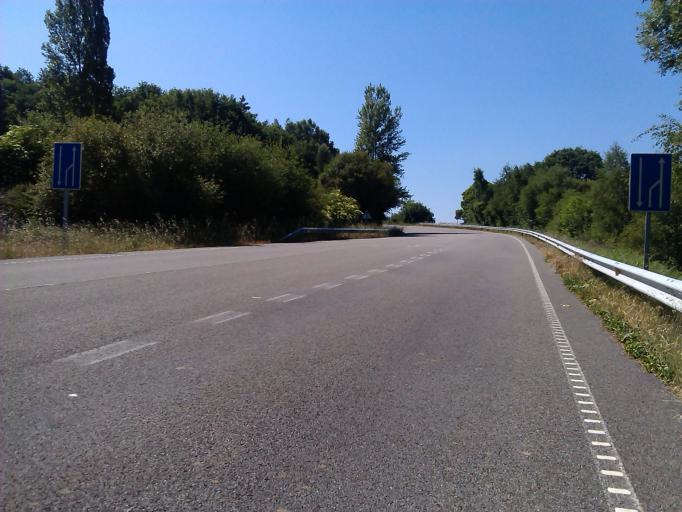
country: ES
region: Galicia
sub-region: Provincia de Lugo
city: Samos
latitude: 42.7338
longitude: -7.3550
